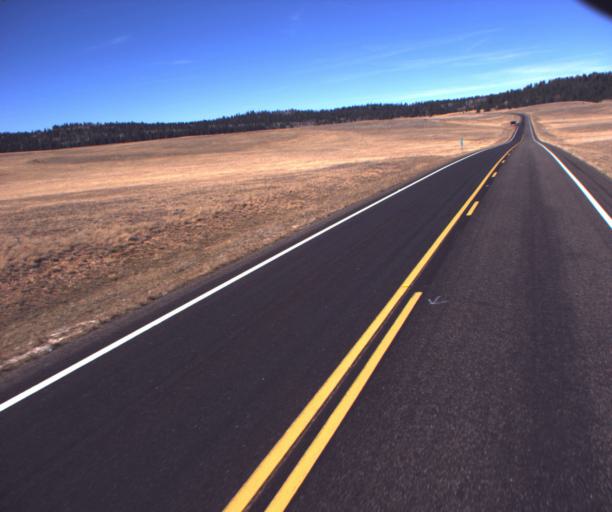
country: US
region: Arizona
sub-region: Coconino County
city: Grand Canyon
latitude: 36.4891
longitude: -112.1300
